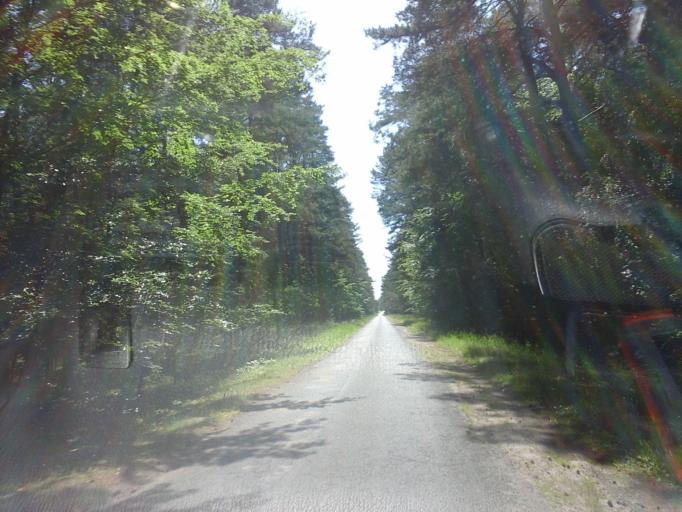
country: PL
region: West Pomeranian Voivodeship
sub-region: Powiat choszczenski
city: Drawno
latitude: 53.1410
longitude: 15.8615
